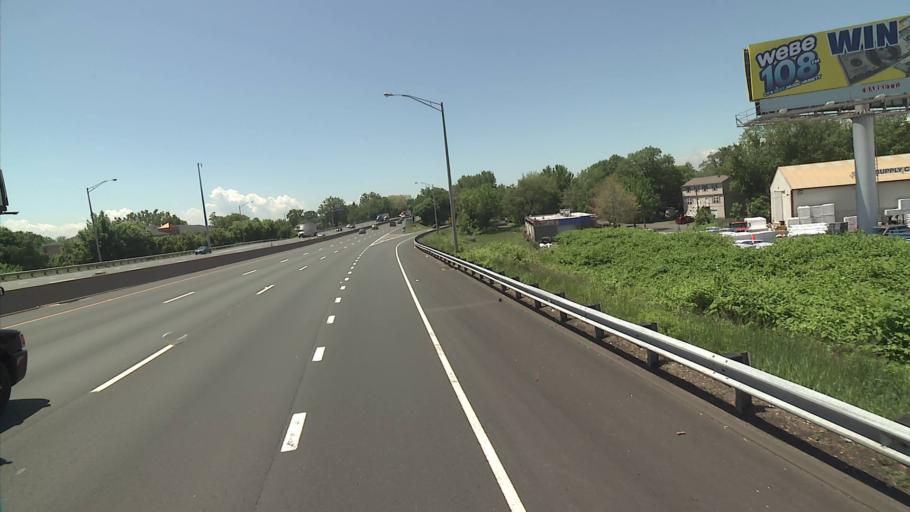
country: US
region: Connecticut
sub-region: Fairfield County
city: Stratford
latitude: 41.1857
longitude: -73.1380
